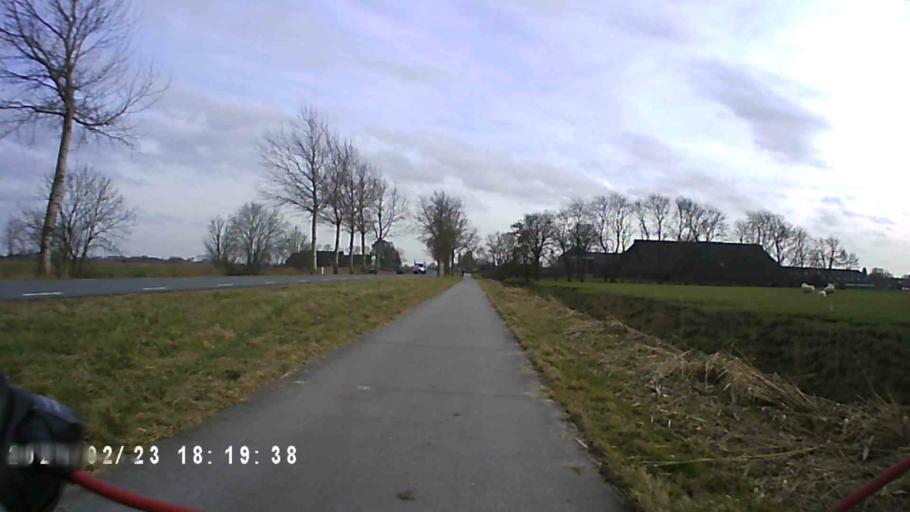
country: NL
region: Groningen
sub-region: Gemeente Bedum
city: Bedum
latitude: 53.3717
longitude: 6.6310
